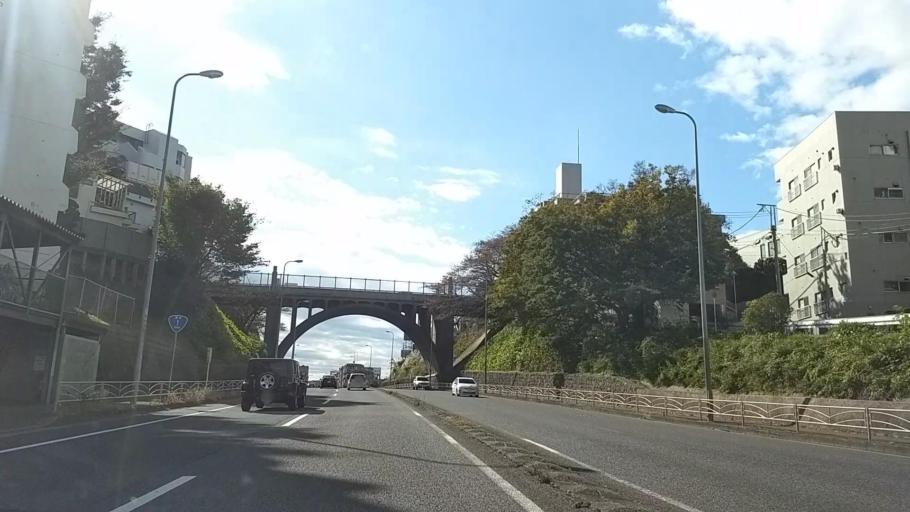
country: JP
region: Kanagawa
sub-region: Kawasaki-shi
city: Kawasaki
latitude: 35.5125
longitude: 139.6634
